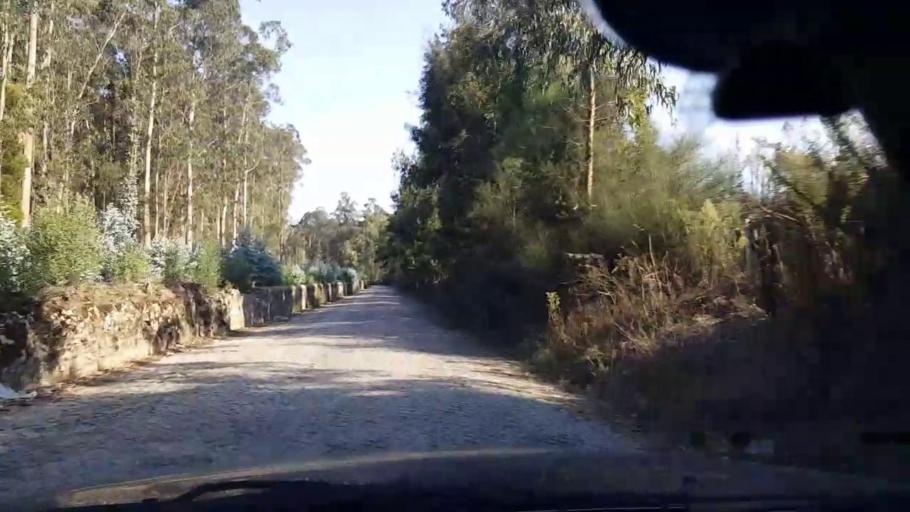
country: PT
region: Porto
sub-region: Vila do Conde
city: Arvore
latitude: 41.3522
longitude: -8.7033
